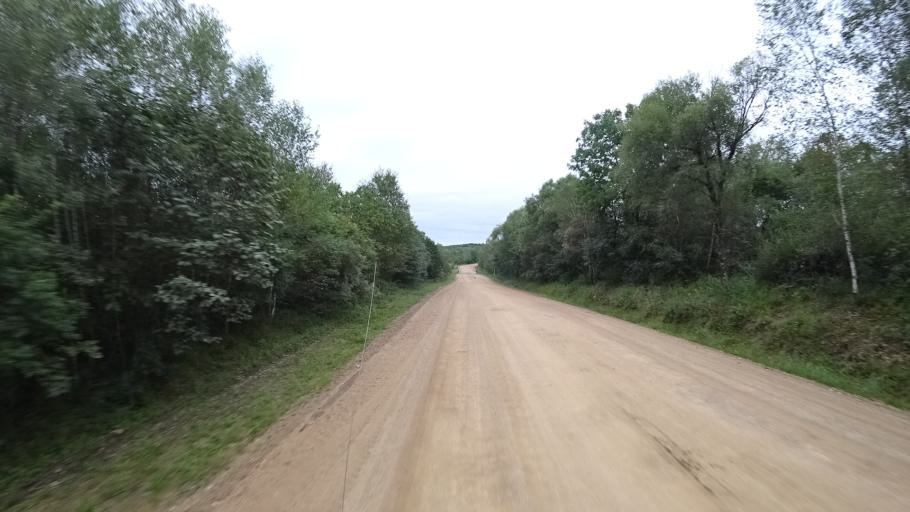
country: RU
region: Primorskiy
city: Rettikhovka
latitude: 44.1722
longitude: 132.7958
